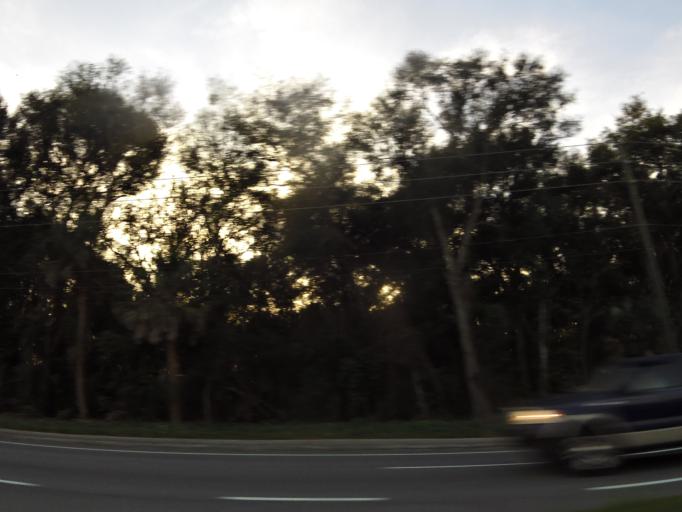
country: US
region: Florida
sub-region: Volusia County
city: North DeLand
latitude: 29.0676
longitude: -81.3047
